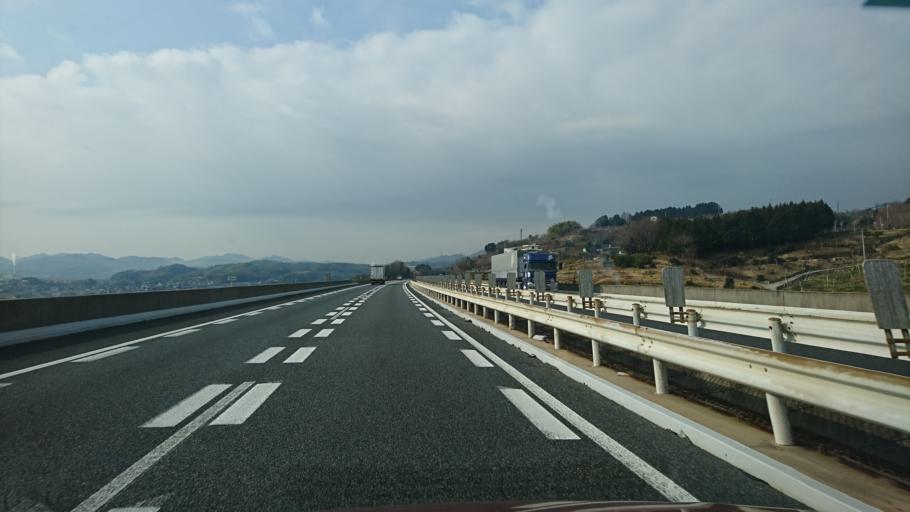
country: JP
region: Okayama
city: Kamogatacho-kamogata
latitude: 34.5698
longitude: 133.6644
